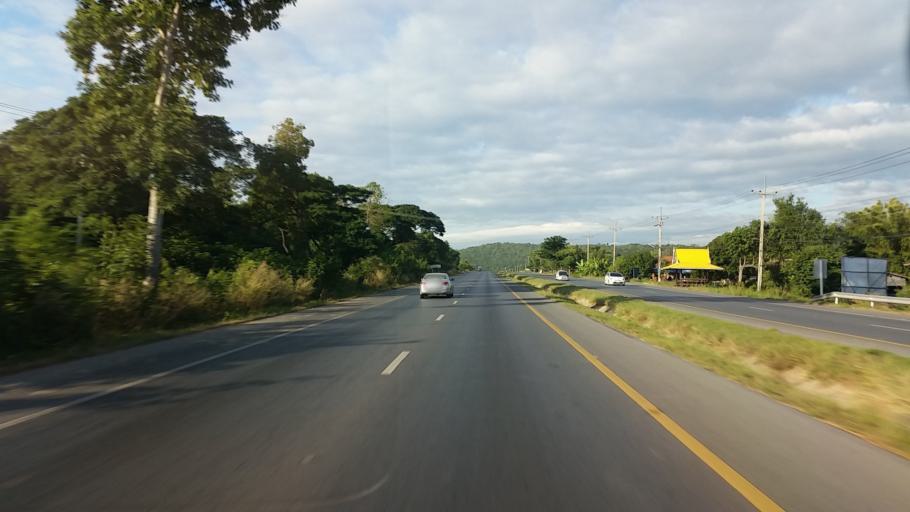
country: TH
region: Lop Buri
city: Phatthana Nikhom
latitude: 14.9828
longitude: 100.9173
